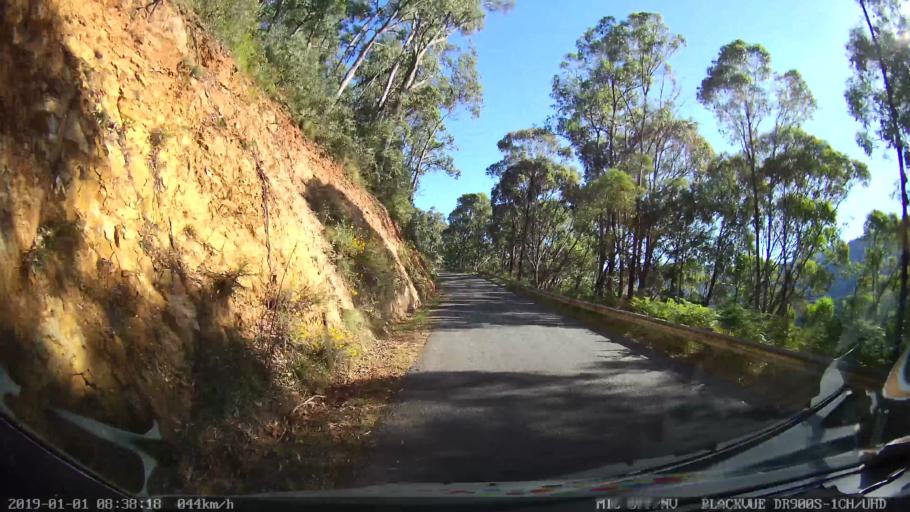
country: AU
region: New South Wales
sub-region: Snowy River
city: Jindabyne
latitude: -36.3331
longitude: 148.1978
